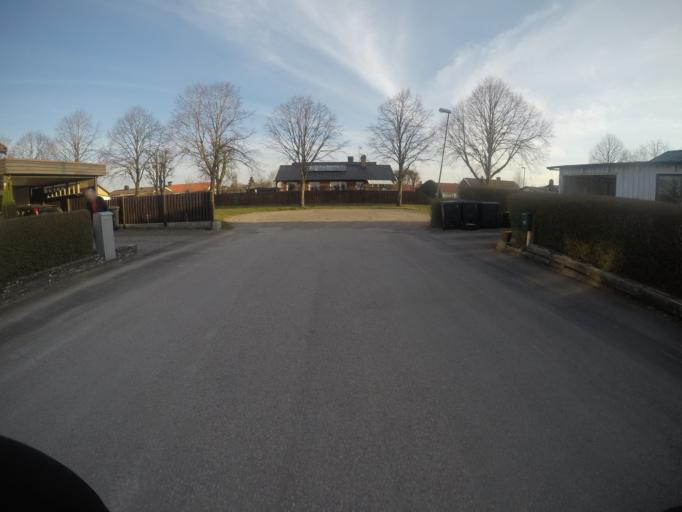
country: SE
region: Halland
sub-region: Laholms Kommun
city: Laholm
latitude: 56.5028
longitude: 13.0257
